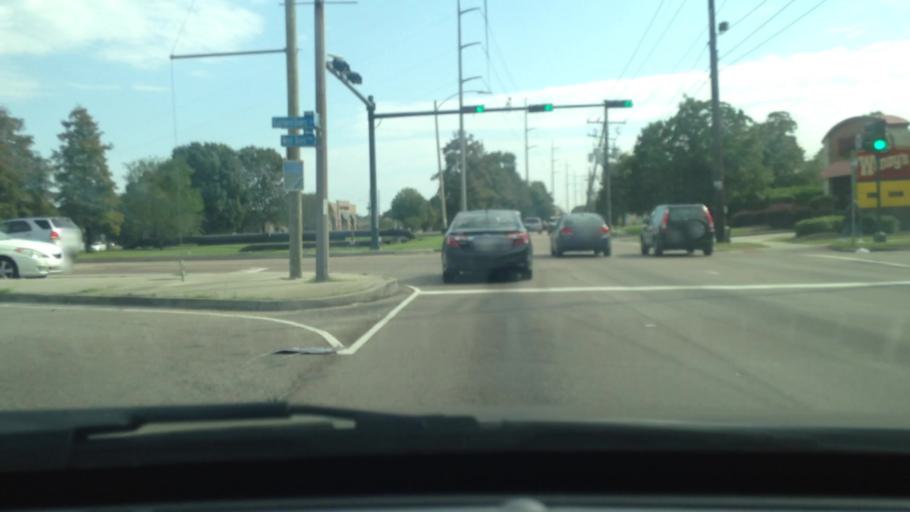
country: US
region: Louisiana
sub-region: Jefferson Parish
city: Terrytown
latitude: 29.9250
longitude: -90.0218
